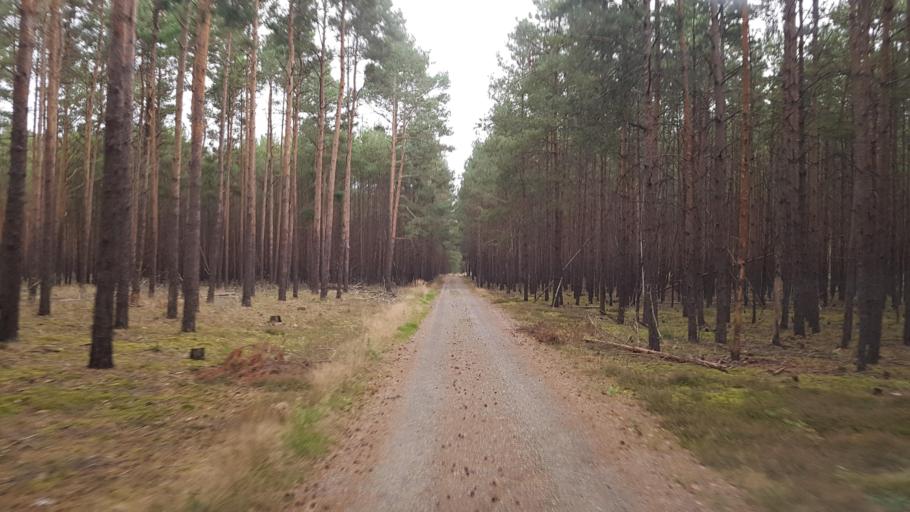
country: DE
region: Brandenburg
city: Sonnewalde
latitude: 51.7372
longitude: 13.6573
